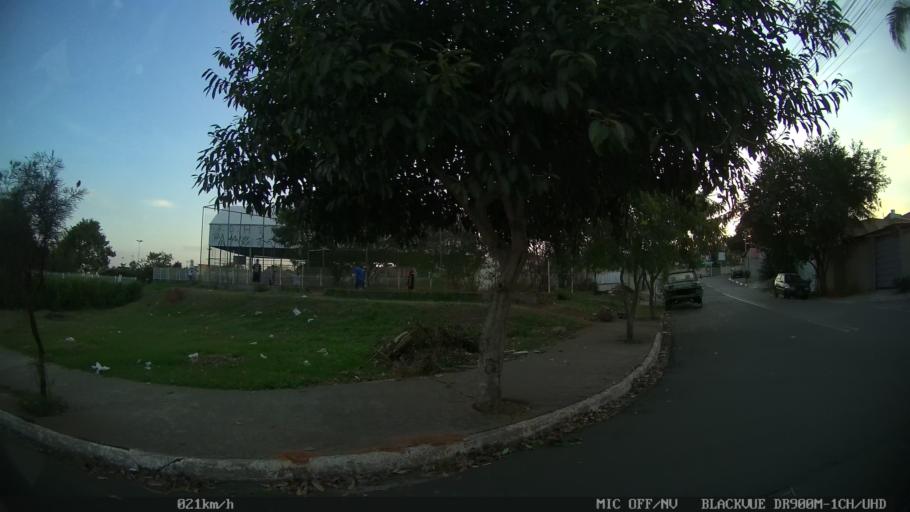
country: BR
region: Sao Paulo
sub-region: Hortolandia
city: Hortolandia
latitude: -22.8504
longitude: -47.2070
